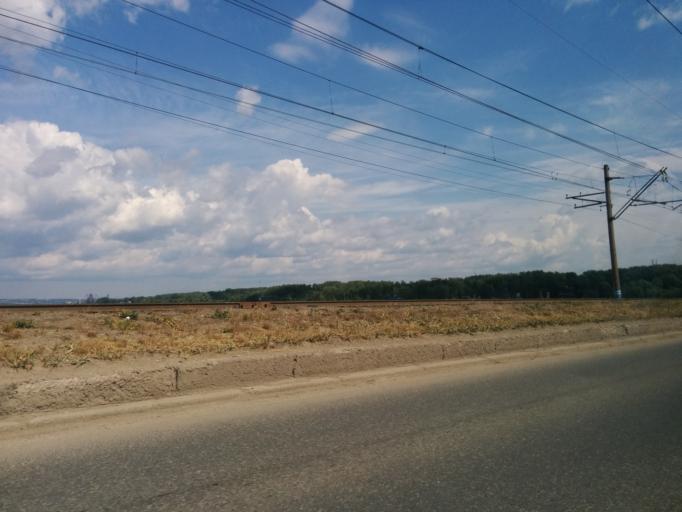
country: RU
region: Perm
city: Perm
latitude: 58.1149
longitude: 56.3574
